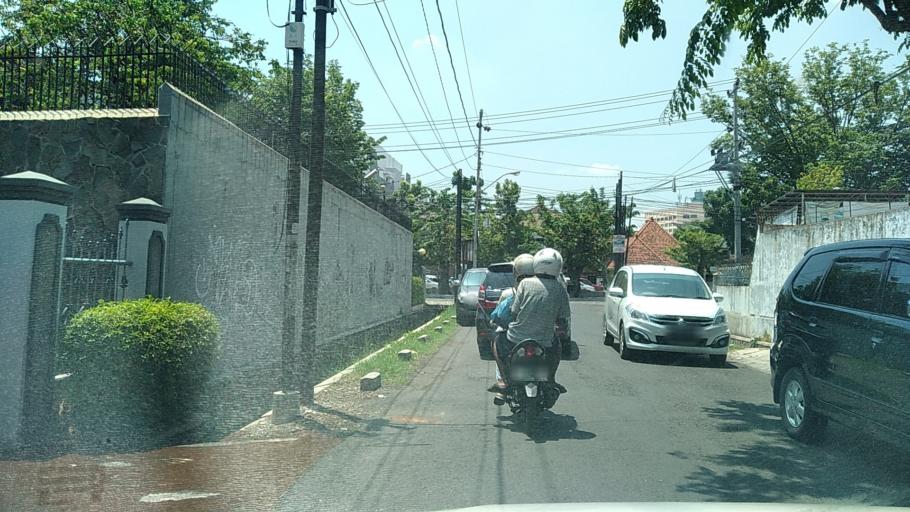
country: ID
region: Central Java
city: Semarang
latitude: -6.9853
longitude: 110.4242
